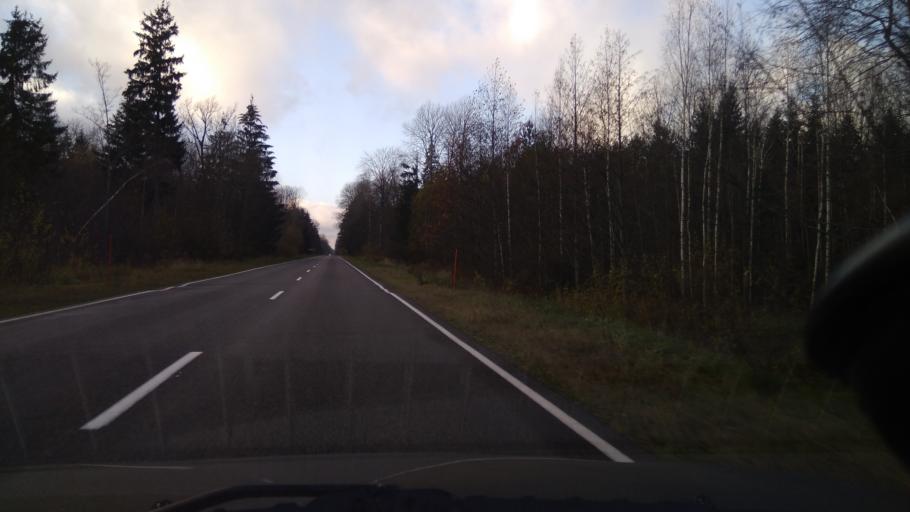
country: BY
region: Minsk
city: Urechcha
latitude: 53.2086
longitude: 27.9091
